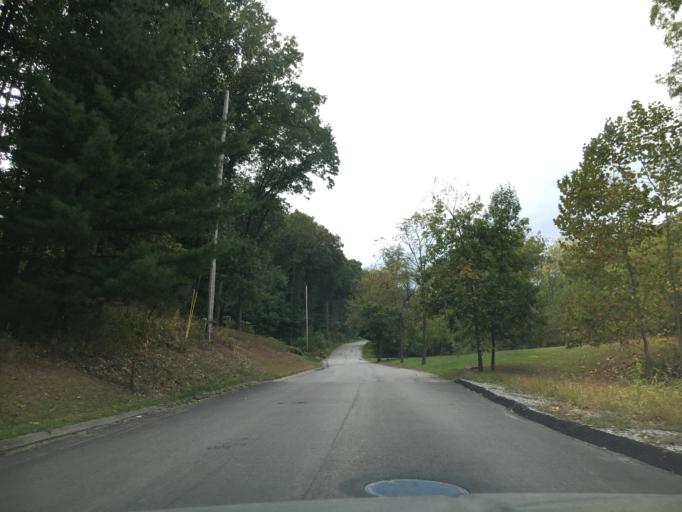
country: US
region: Pennsylvania
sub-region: York County
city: Grantley
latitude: 39.9354
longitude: -76.7192
